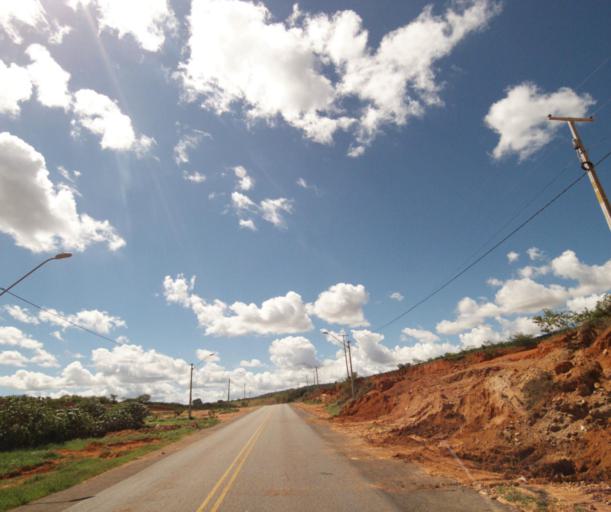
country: BR
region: Bahia
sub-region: Cacule
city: Cacule
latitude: -14.2037
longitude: -42.1242
